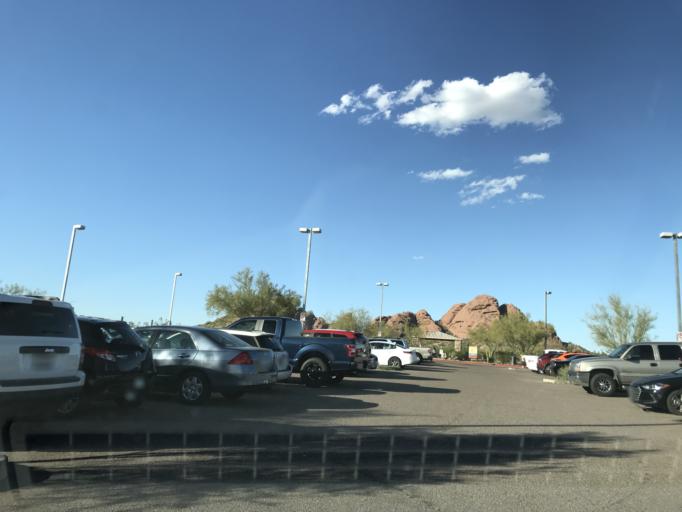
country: US
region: Arizona
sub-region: Maricopa County
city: Tempe Junction
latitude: 33.4547
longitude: -111.9545
